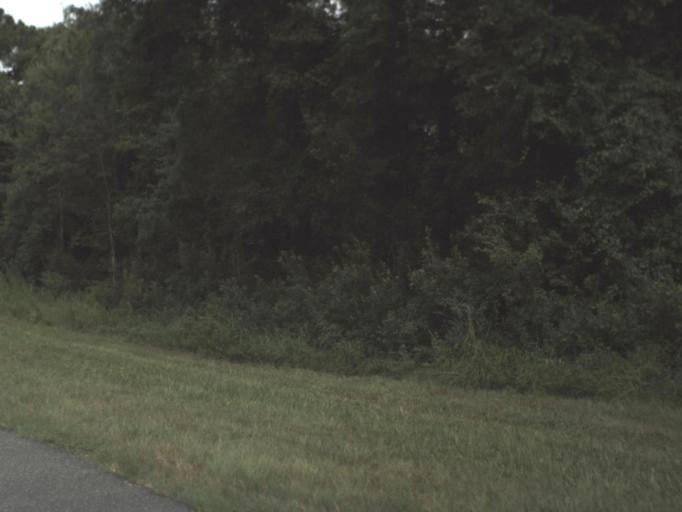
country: US
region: Florida
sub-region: Taylor County
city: Perry
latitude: 30.1131
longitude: -83.4165
